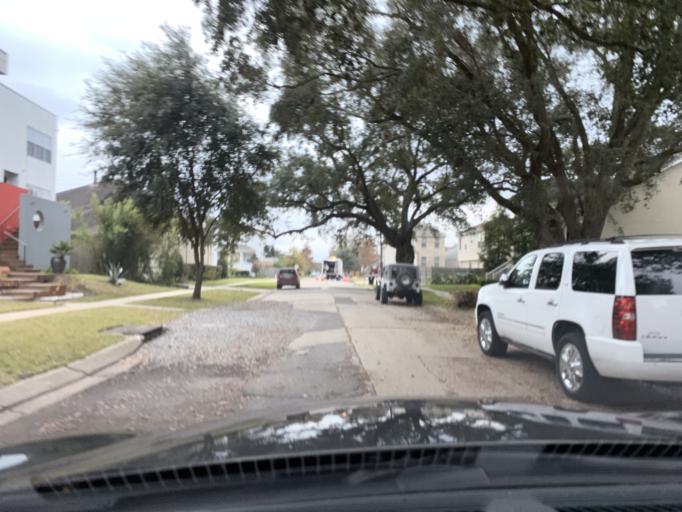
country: US
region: Louisiana
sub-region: Jefferson Parish
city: Metairie
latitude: 30.0144
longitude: -90.1036
